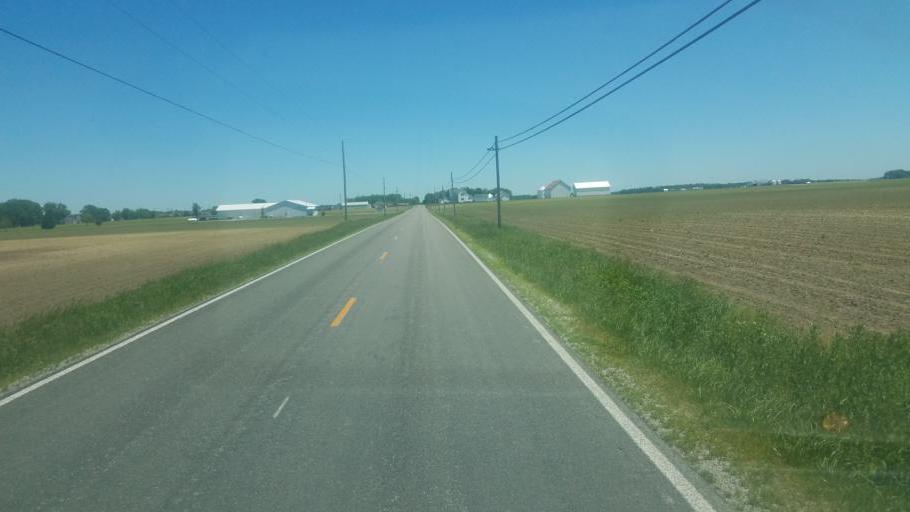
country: US
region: Ohio
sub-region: Darke County
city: Versailles
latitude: 40.2264
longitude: -84.4264
